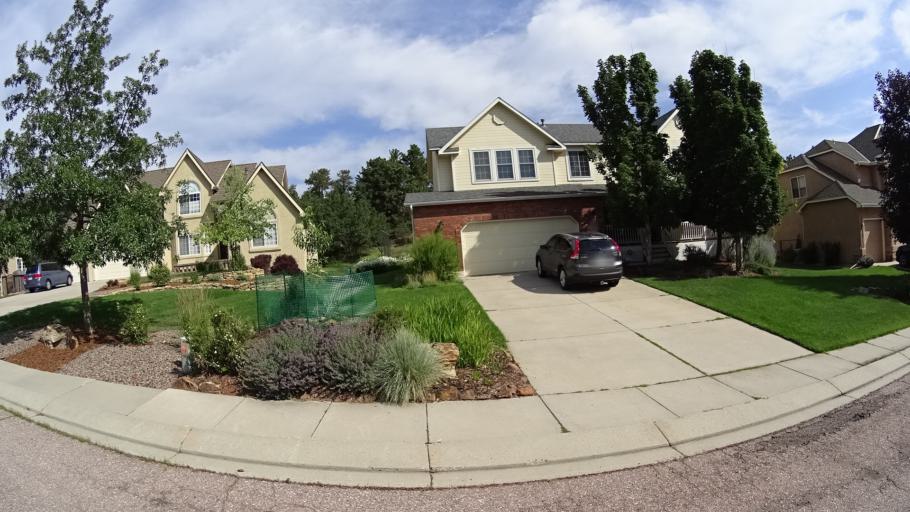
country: US
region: Colorado
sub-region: El Paso County
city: Air Force Academy
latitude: 38.9429
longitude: -104.8644
